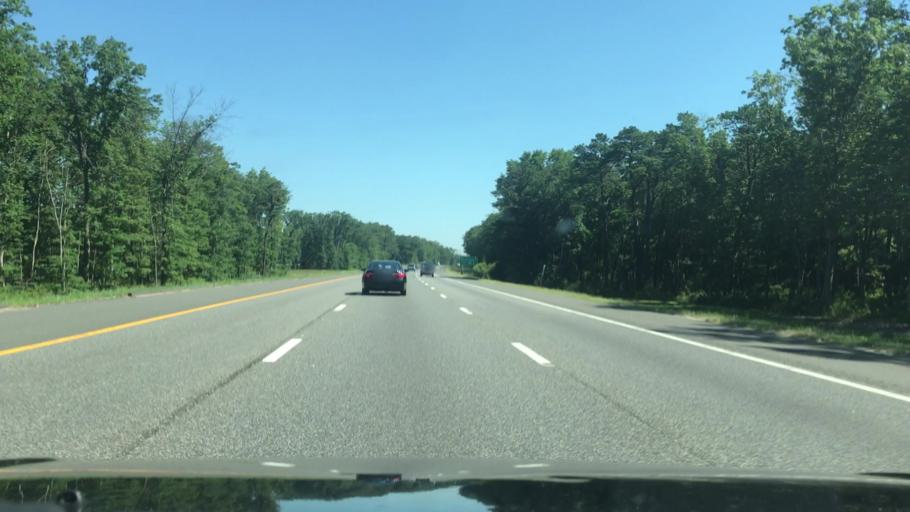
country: US
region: New Jersey
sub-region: Ocean County
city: Leisure Village
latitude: 40.0311
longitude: -74.1826
